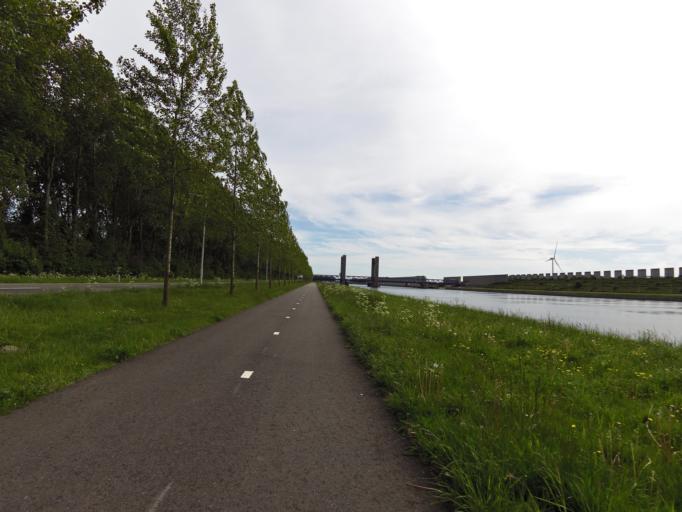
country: NL
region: South Holland
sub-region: Gemeente Maassluis
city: Maassluis
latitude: 51.9080
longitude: 4.2270
